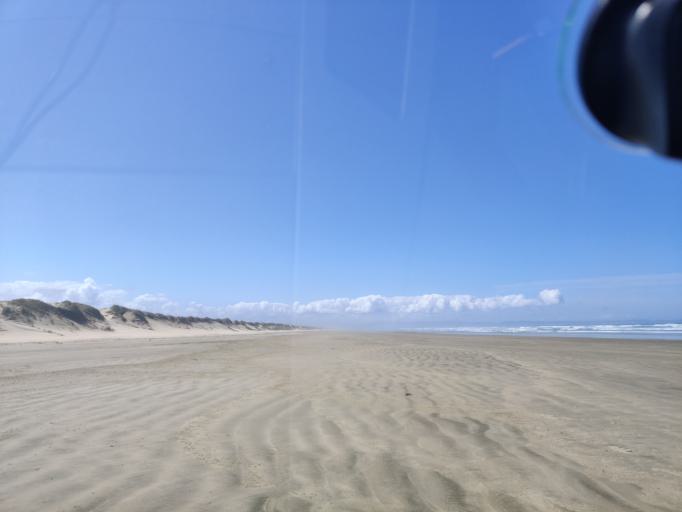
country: NZ
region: Northland
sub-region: Far North District
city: Kaitaia
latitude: -34.9266
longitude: 173.1052
